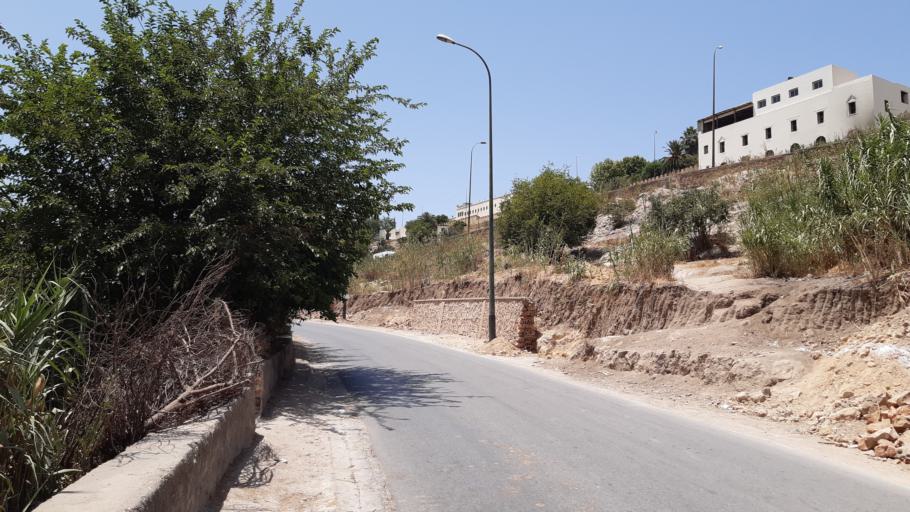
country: MA
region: Fes-Boulemane
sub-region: Fes
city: Fes
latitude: 34.0562
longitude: -4.9771
